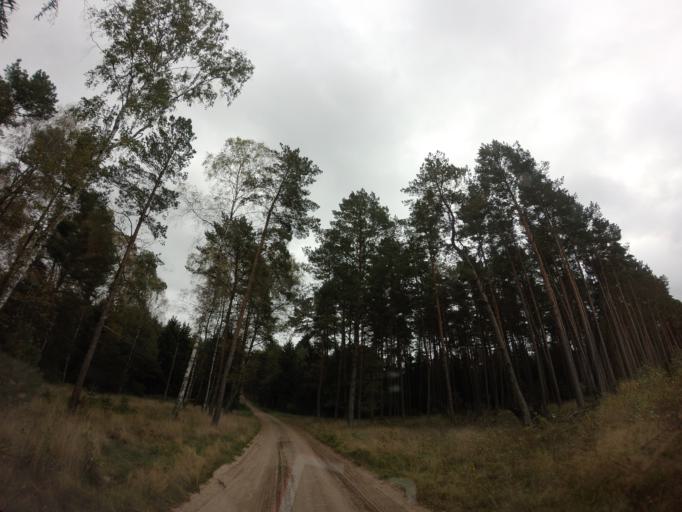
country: PL
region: West Pomeranian Voivodeship
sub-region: Powiat choszczenski
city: Drawno
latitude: 53.1397
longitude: 15.7198
